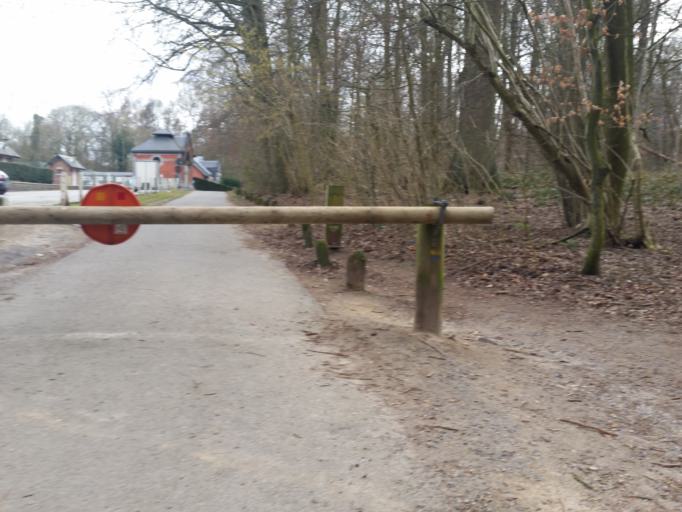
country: BE
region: Flanders
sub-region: Provincie Vlaams-Brabant
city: Sint-Genesius-Rode
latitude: 50.7918
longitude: 4.3870
